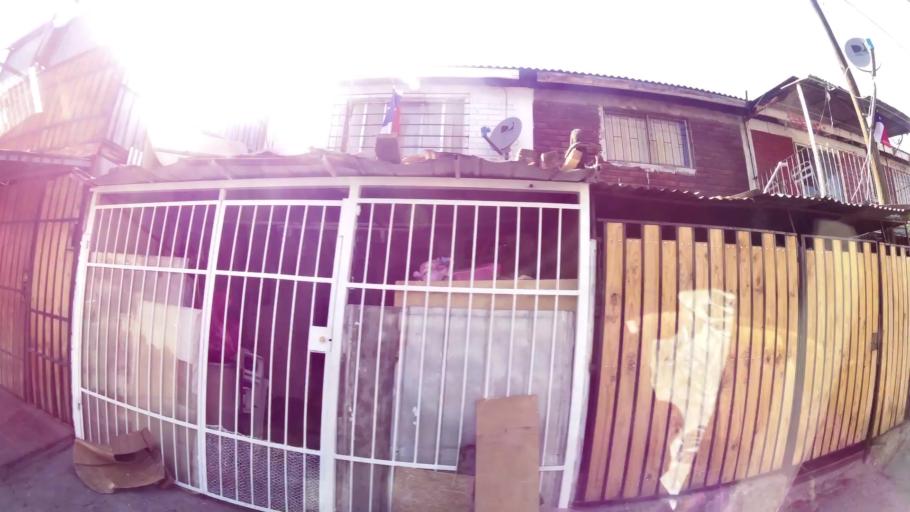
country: CL
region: Santiago Metropolitan
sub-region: Provincia de Santiago
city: La Pintana
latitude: -33.5641
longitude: -70.6401
